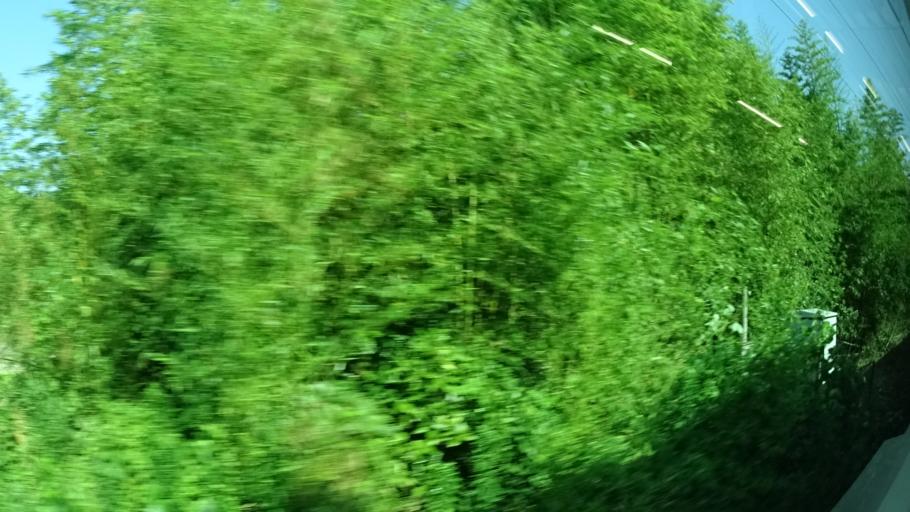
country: JP
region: Miyagi
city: Matsushima
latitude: 38.4014
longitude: 141.0657
